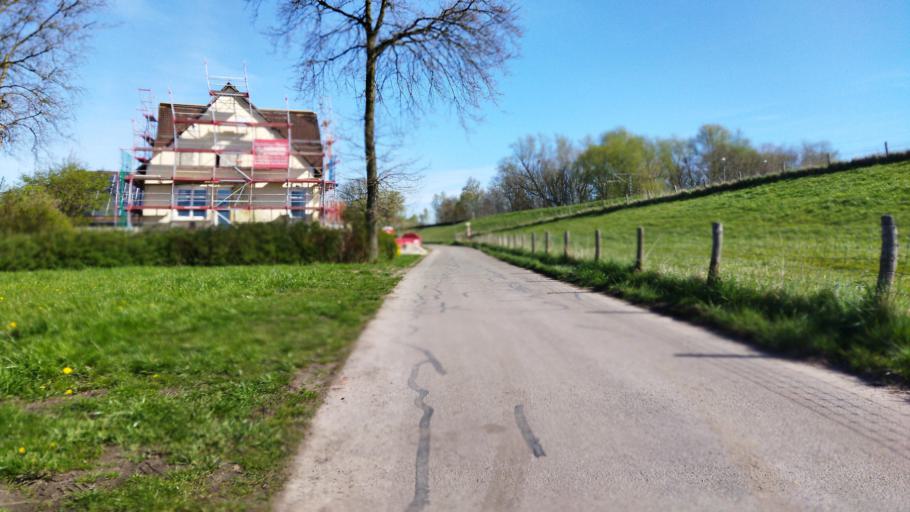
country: DE
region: Lower Saxony
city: Elsfleth
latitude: 53.2247
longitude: 8.4552
